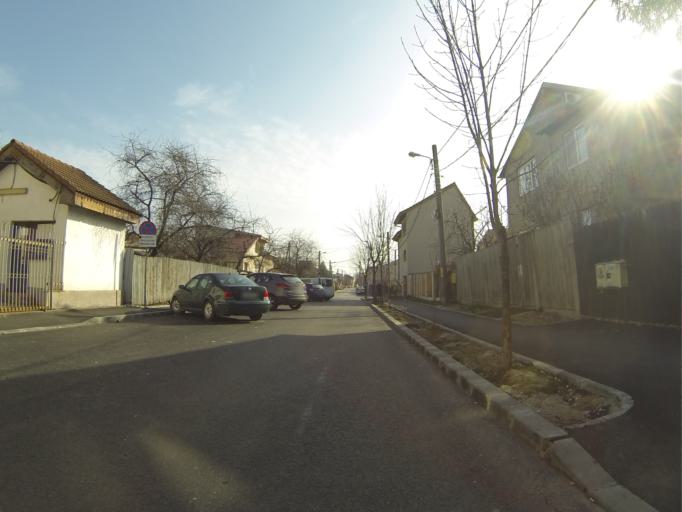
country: RO
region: Dolj
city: Craiova
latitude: 44.3123
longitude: 23.8116
